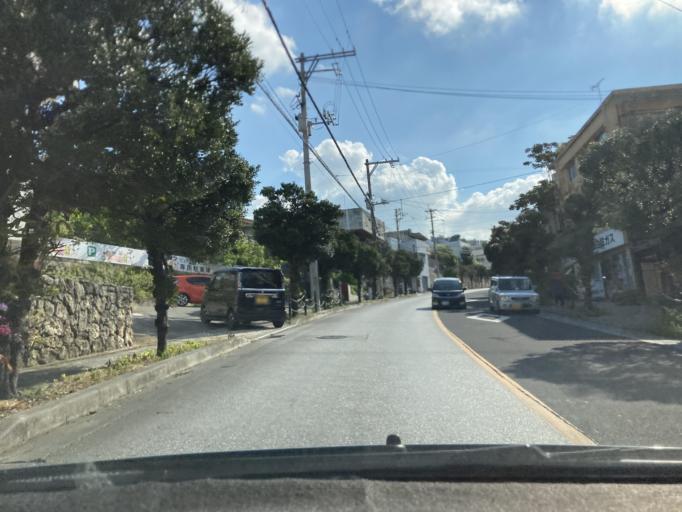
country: JP
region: Okinawa
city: Naha-shi
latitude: 26.2140
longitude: 127.7156
